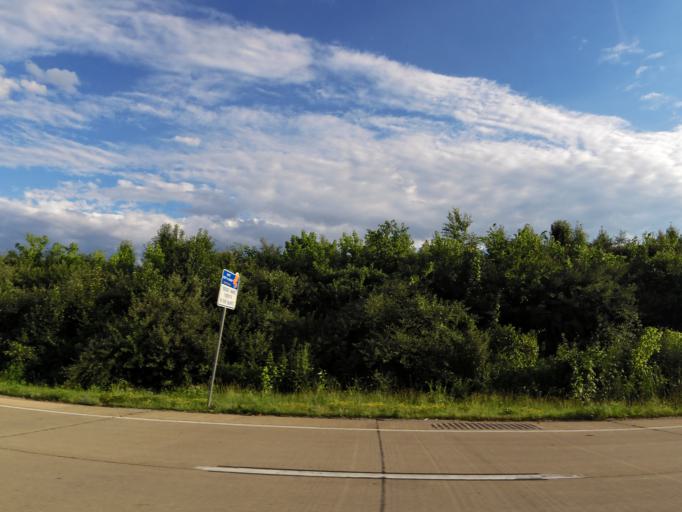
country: US
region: Missouri
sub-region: Saint Charles County
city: Weldon Spring
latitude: 38.7116
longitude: -90.6902
